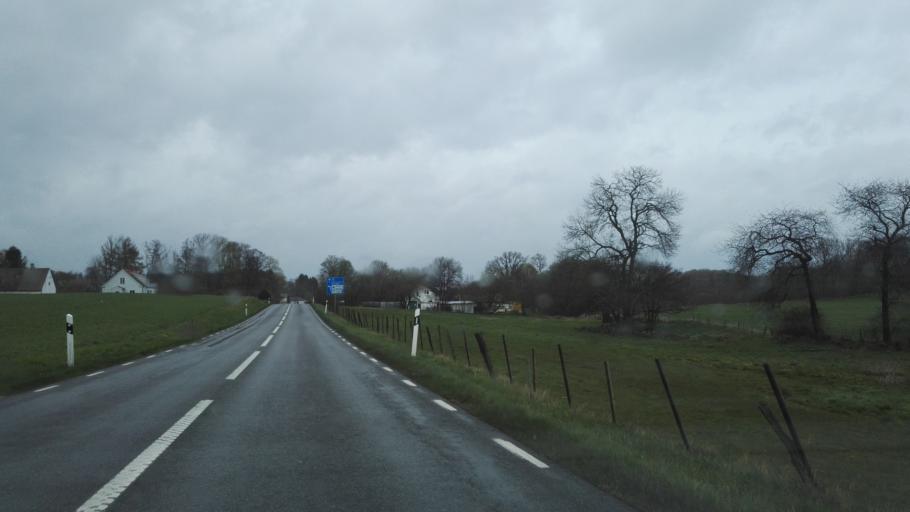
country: SE
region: Skane
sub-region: Simrishamns Kommun
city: Kivik
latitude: 55.6703
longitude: 14.2228
